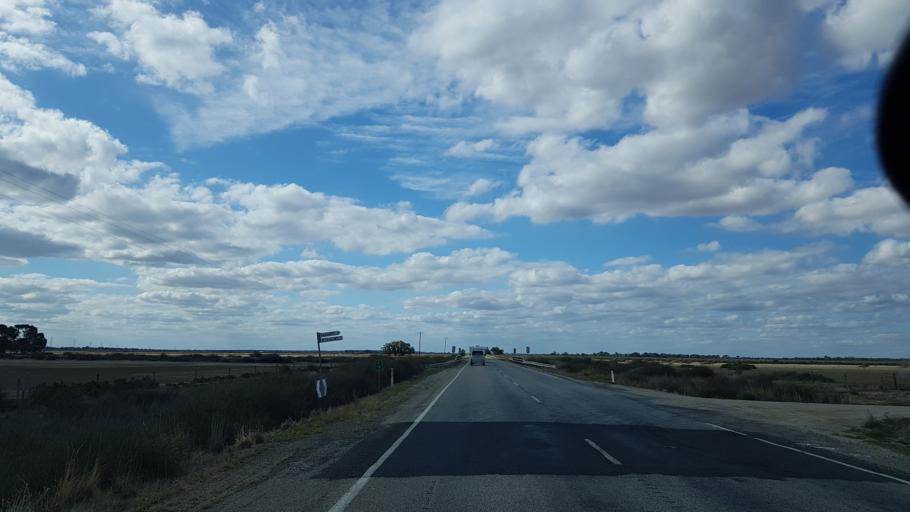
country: AU
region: Victoria
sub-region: Swan Hill
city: Swan Hill
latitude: -35.8566
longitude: 143.9360
